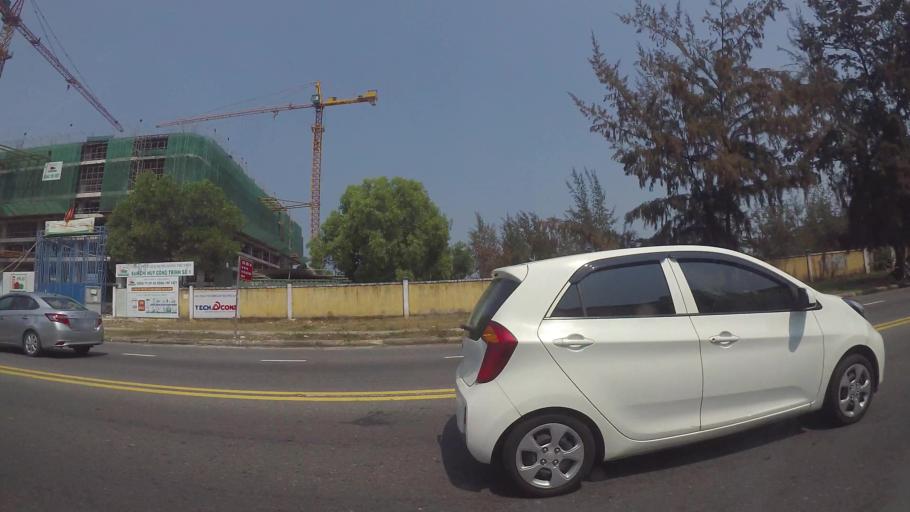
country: VN
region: Da Nang
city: Ngu Hanh Son
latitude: 16.0030
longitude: 108.2669
